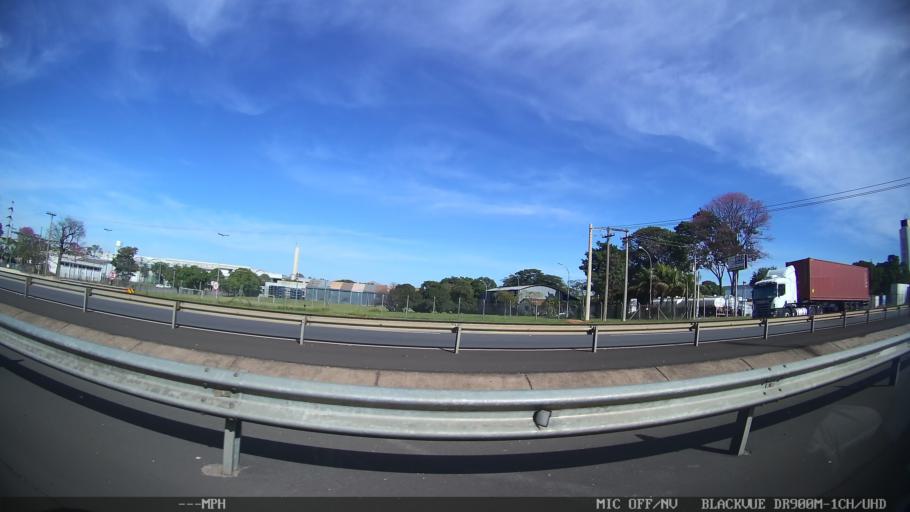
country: BR
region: Sao Paulo
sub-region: Limeira
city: Limeira
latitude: -22.5479
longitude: -47.3720
